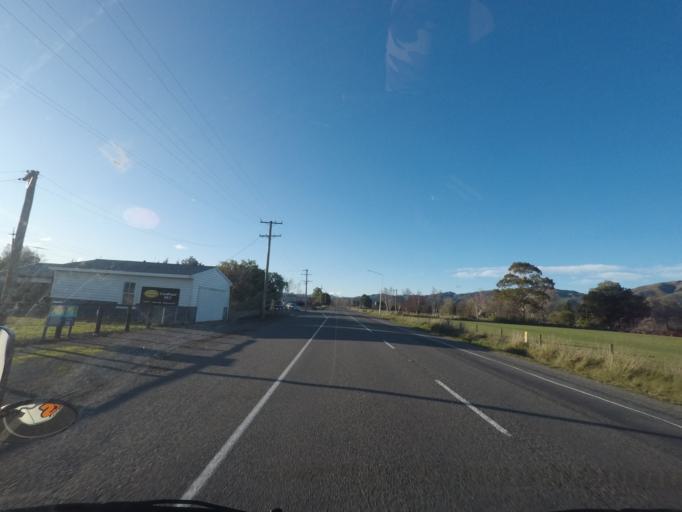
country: NZ
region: Canterbury
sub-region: Kaikoura District
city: Kaikoura
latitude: -42.7137
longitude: 173.2903
